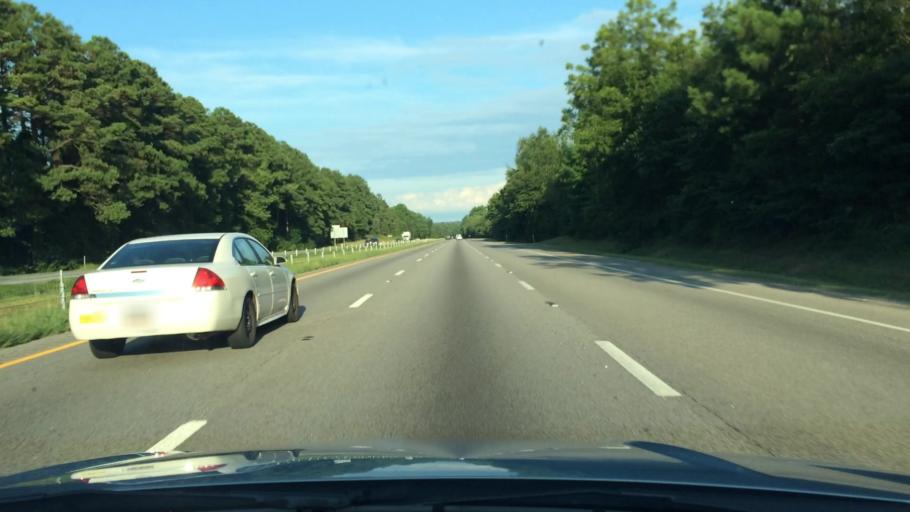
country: US
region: South Carolina
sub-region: Newberry County
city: Prosperity
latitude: 34.2378
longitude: -81.4575
